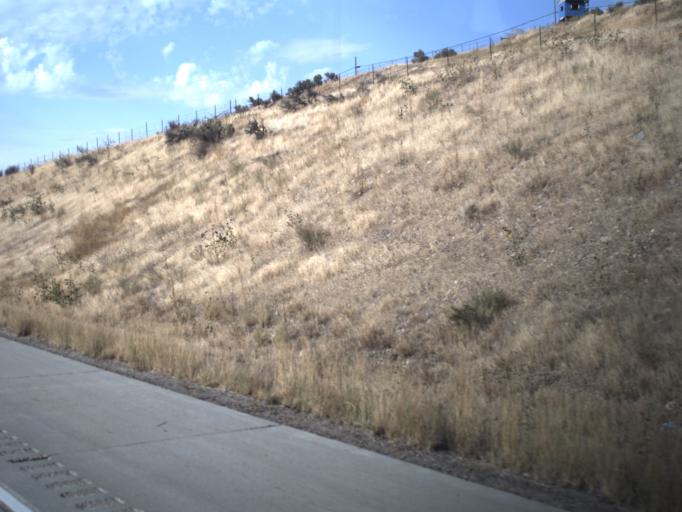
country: US
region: Utah
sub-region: Morgan County
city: Morgan
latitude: 41.0859
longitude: -111.7325
